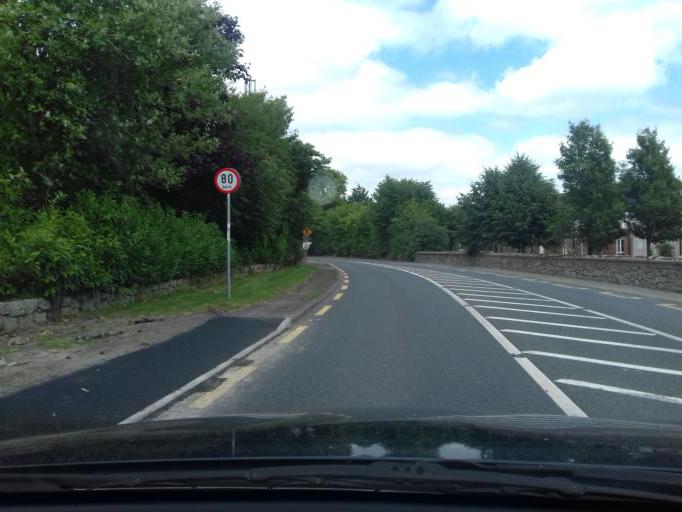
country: IE
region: Leinster
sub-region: County Carlow
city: Tullow
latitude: 52.8093
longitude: -6.7275
